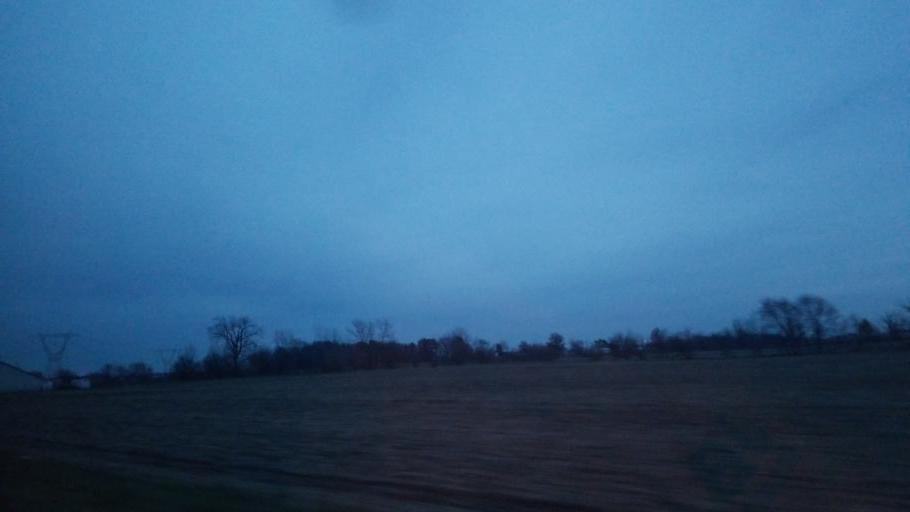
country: US
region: Indiana
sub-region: Adams County
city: Berne
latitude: 40.7154
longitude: -84.9868
